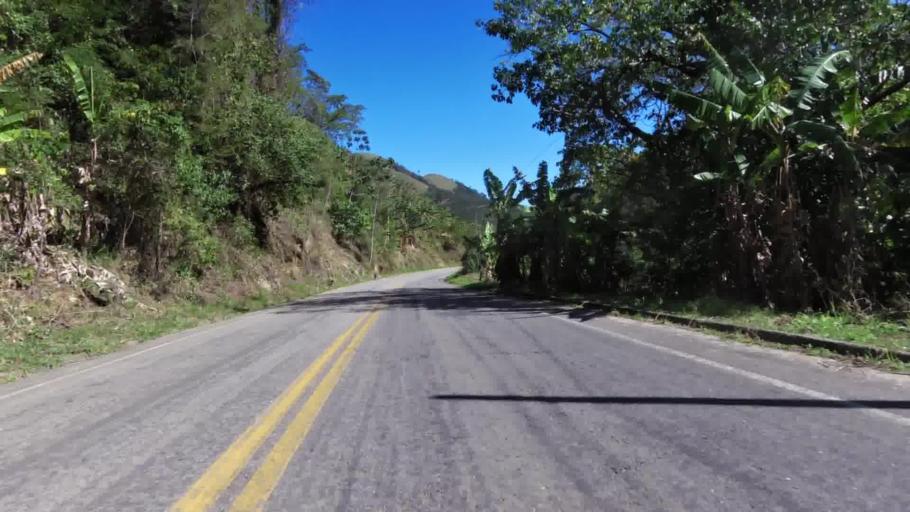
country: BR
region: Espirito Santo
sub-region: Iconha
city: Iconha
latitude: -20.7476
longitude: -40.8601
